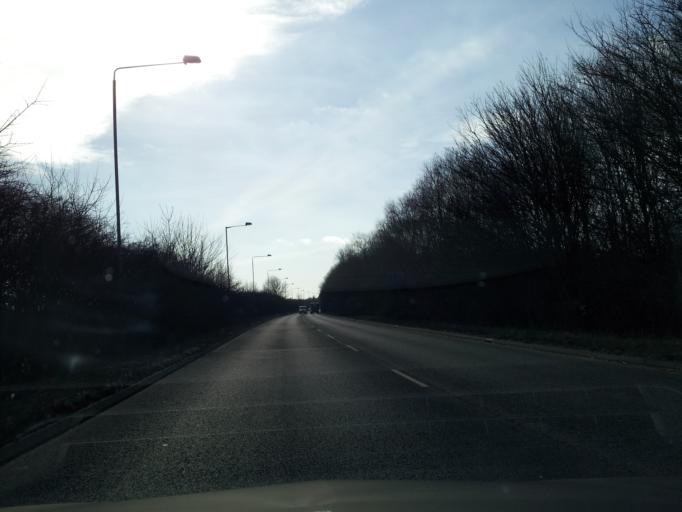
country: GB
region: England
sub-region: Nottinghamshire
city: West Bridgford
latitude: 52.9185
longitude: -1.0992
